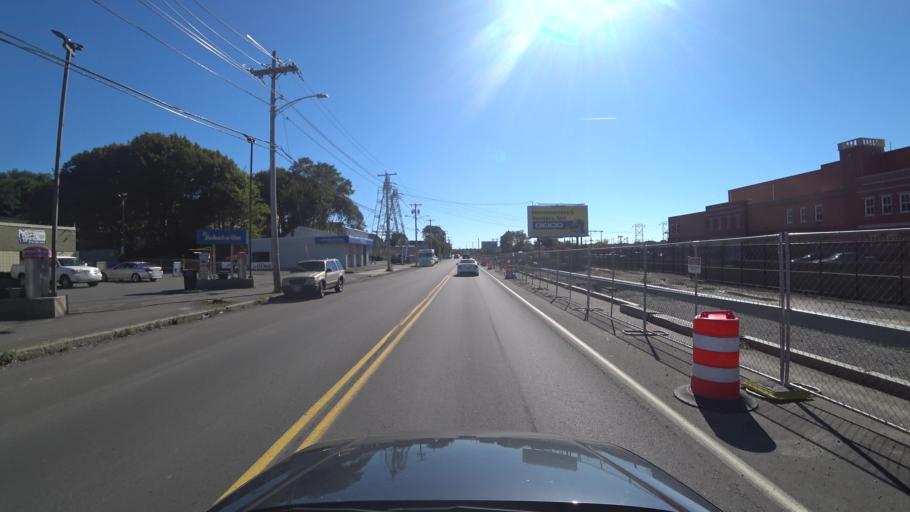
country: US
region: Massachusetts
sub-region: Essex County
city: Salem
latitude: 42.5161
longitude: -70.8959
